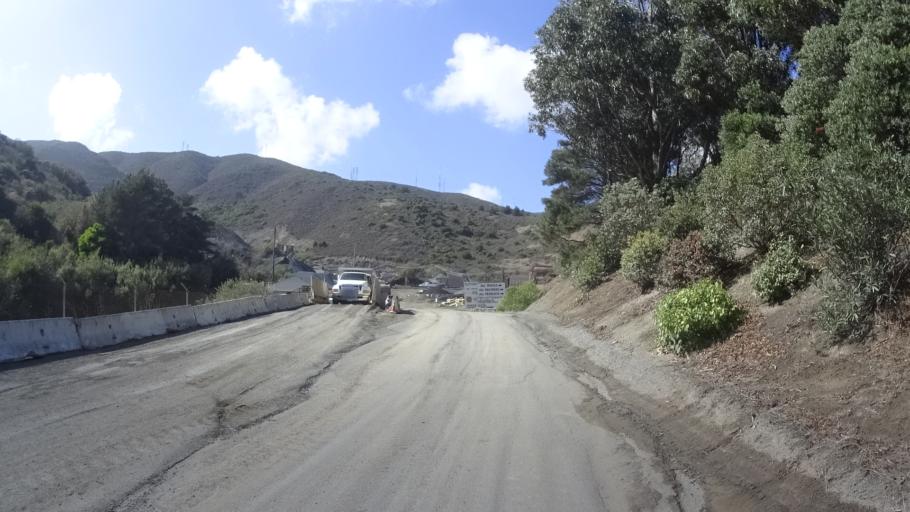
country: US
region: California
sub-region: San Mateo County
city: Brisbane
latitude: 37.6873
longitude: -122.4183
